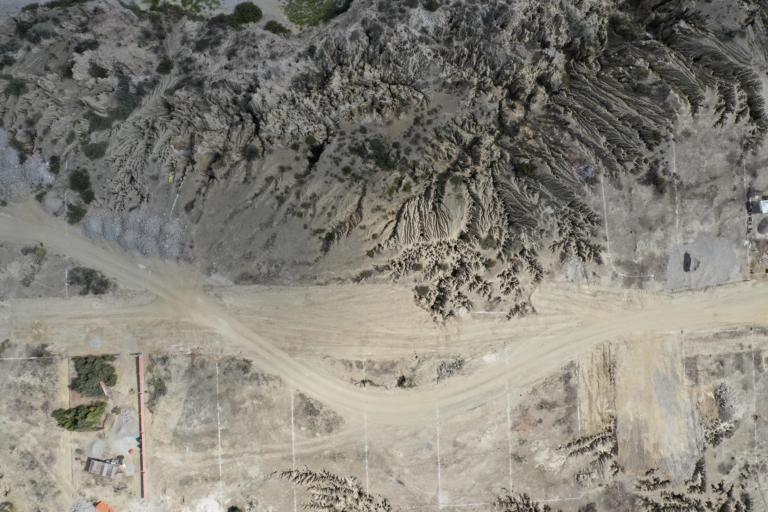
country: BO
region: La Paz
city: La Paz
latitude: -16.5647
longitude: -68.1210
